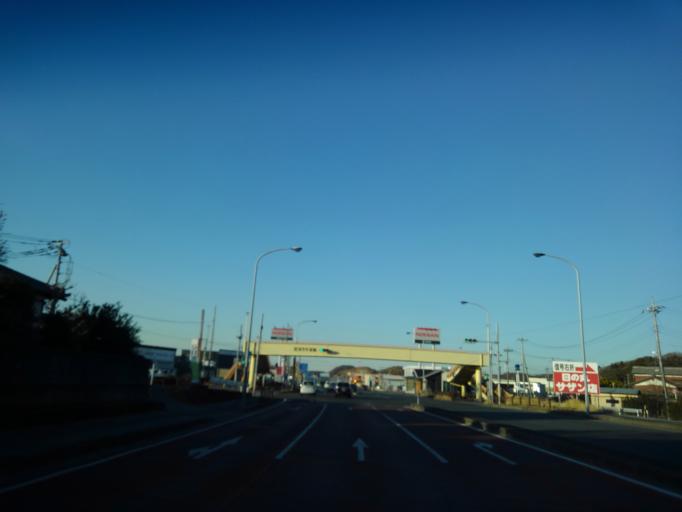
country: JP
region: Chiba
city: Kimitsu
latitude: 35.3158
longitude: 139.9271
